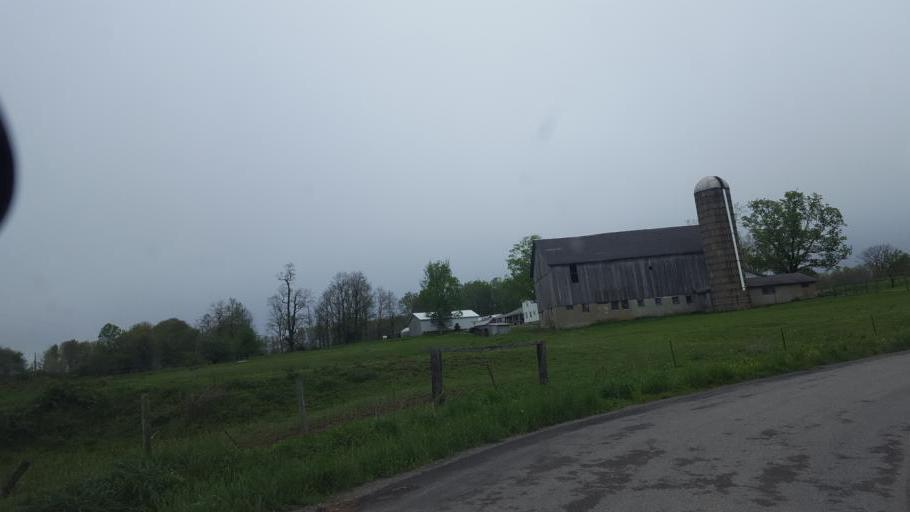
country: US
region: Pennsylvania
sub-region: Mercer County
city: Stoneboro
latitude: 41.3035
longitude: -80.1557
